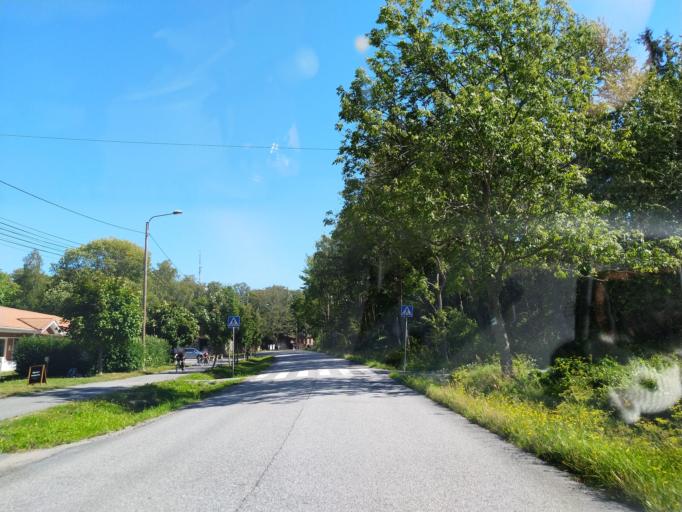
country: FI
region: Varsinais-Suomi
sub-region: Aboland-Turunmaa
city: Dragsfjaerd
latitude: 60.0219
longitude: 22.5026
